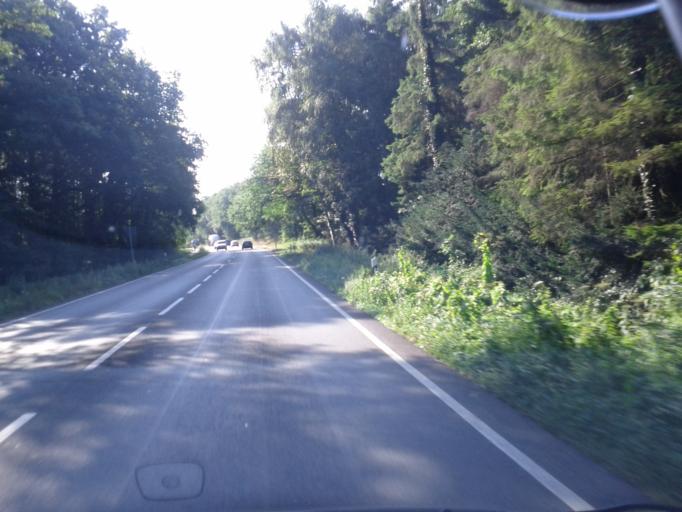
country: DE
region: Lower Saxony
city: Nottensdorf
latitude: 53.4954
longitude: 9.5980
